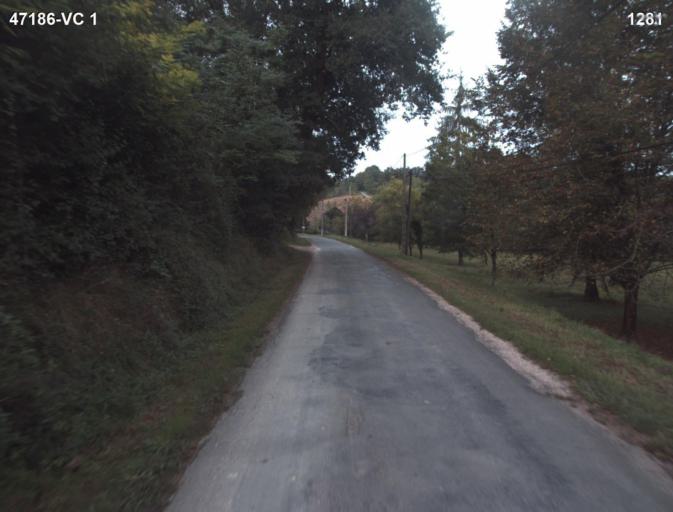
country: FR
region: Aquitaine
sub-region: Departement du Lot-et-Garonne
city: Port-Sainte-Marie
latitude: 44.1986
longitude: 0.4379
